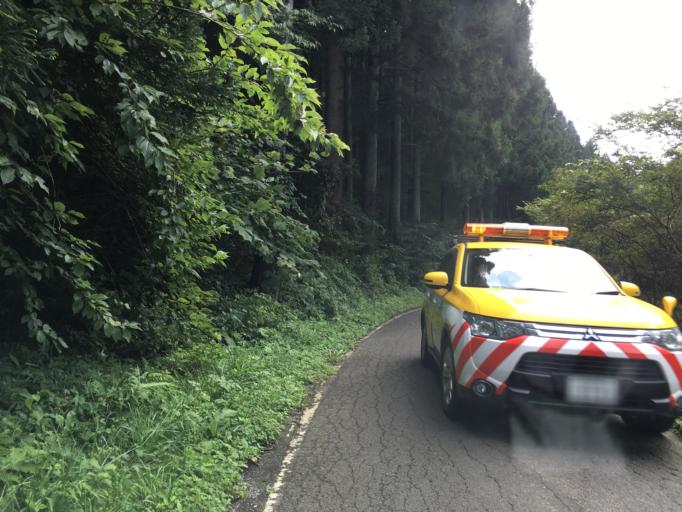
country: JP
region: Miyagi
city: Marumori
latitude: 37.8857
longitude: 140.8671
